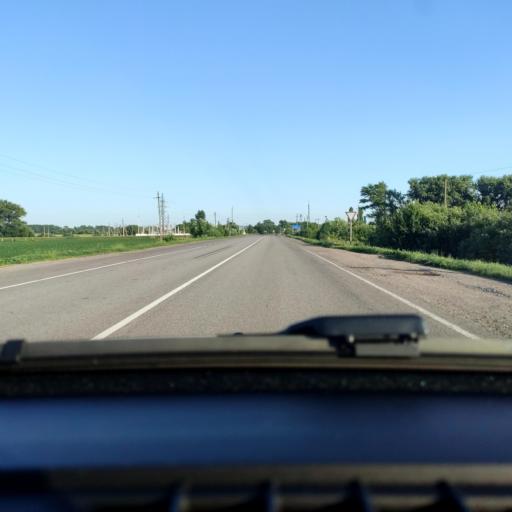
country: RU
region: Voronezj
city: Kashirskoye
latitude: 51.4695
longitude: 39.8627
